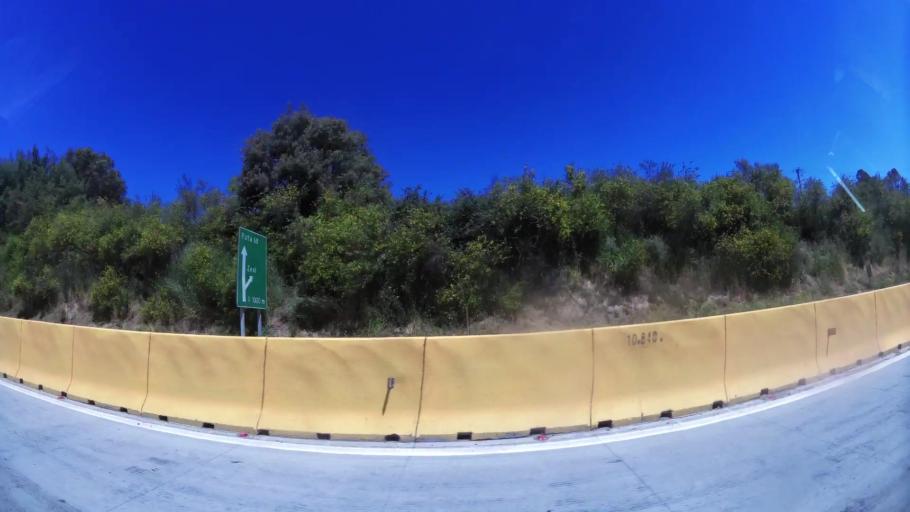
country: CL
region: Valparaiso
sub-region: Provincia de Valparaiso
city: Valparaiso
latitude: -33.0669
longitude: -71.6400
